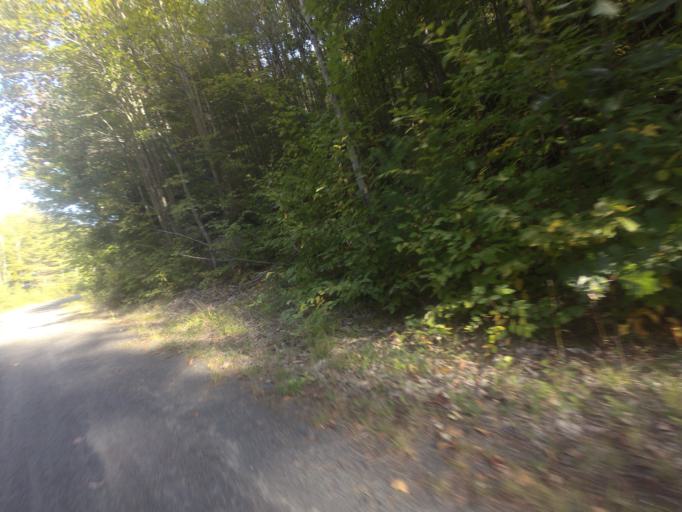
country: CA
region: Quebec
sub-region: Laurentides
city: Sainte-Adele
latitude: 45.9869
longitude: -74.1171
